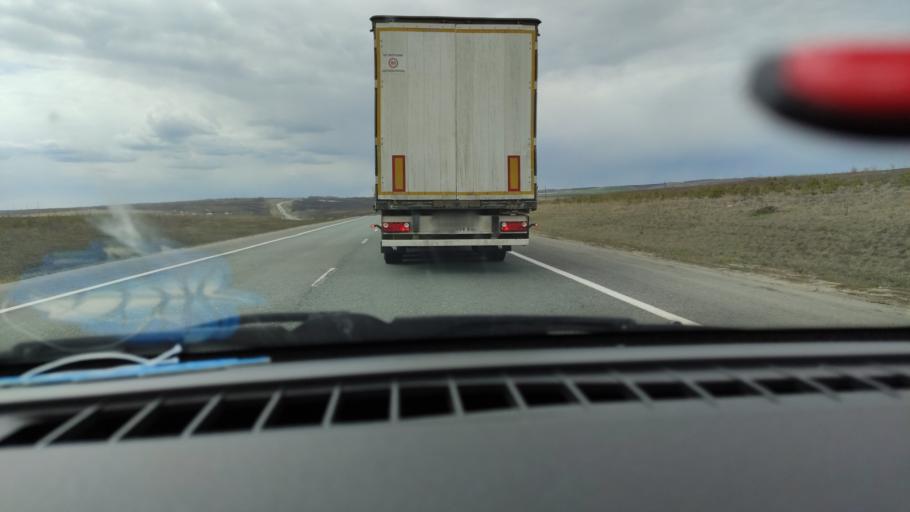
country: RU
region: Saratov
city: Yelshanka
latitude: 51.8287
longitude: 46.4021
